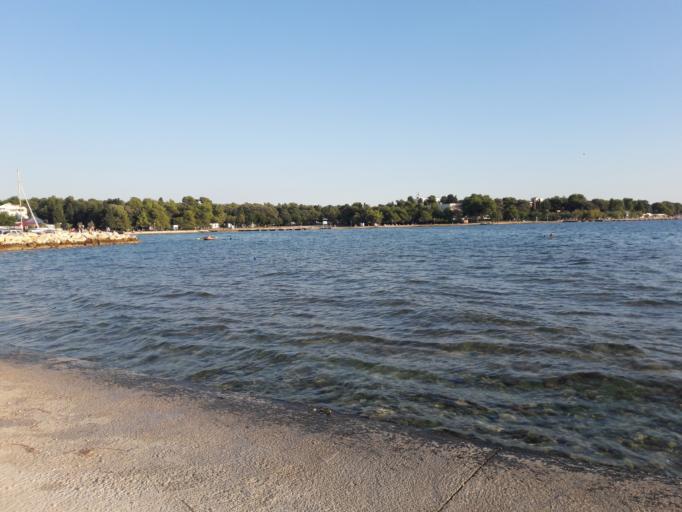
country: HR
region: Zadarska
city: Zadar
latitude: 44.1404
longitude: 15.2115
